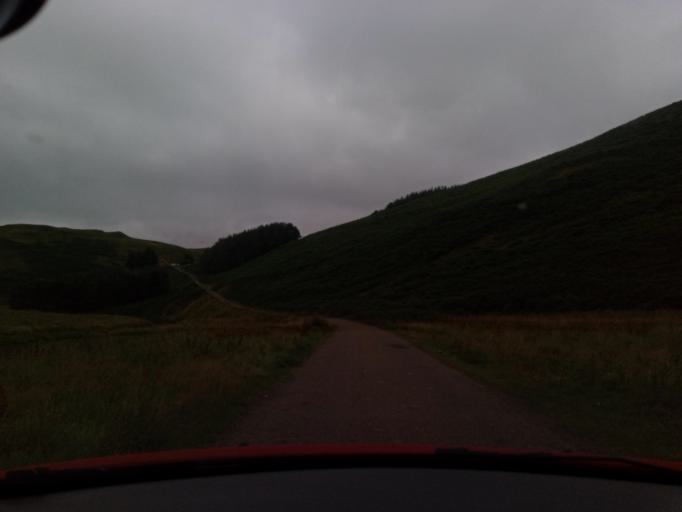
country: GB
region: England
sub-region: Northumberland
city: Rochester
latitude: 55.3723
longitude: -2.2155
